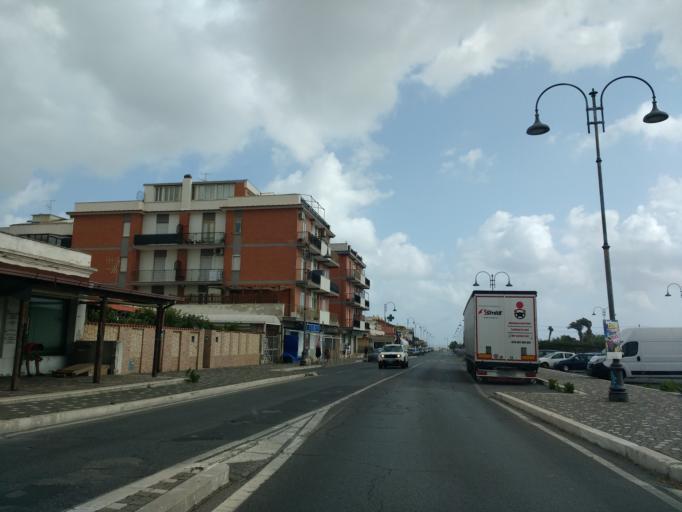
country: IT
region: Latium
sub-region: Citta metropolitana di Roma Capitale
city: Anzio
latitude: 41.4656
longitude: 12.6110
